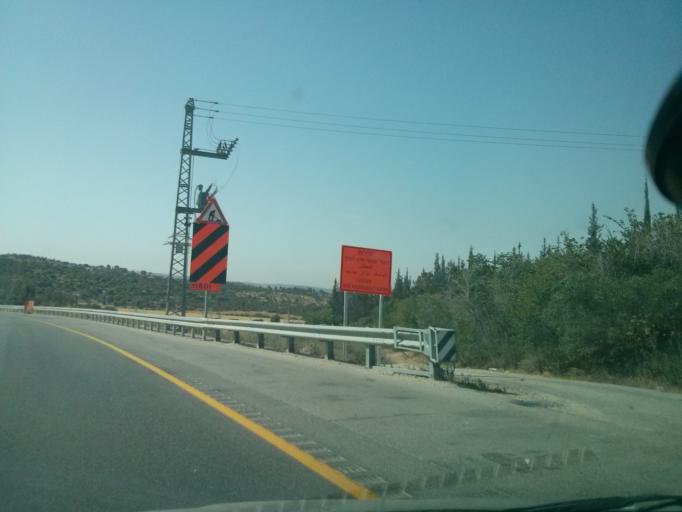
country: IL
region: Jerusalem
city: Bet Shemesh
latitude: 31.6977
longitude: 35.0095
